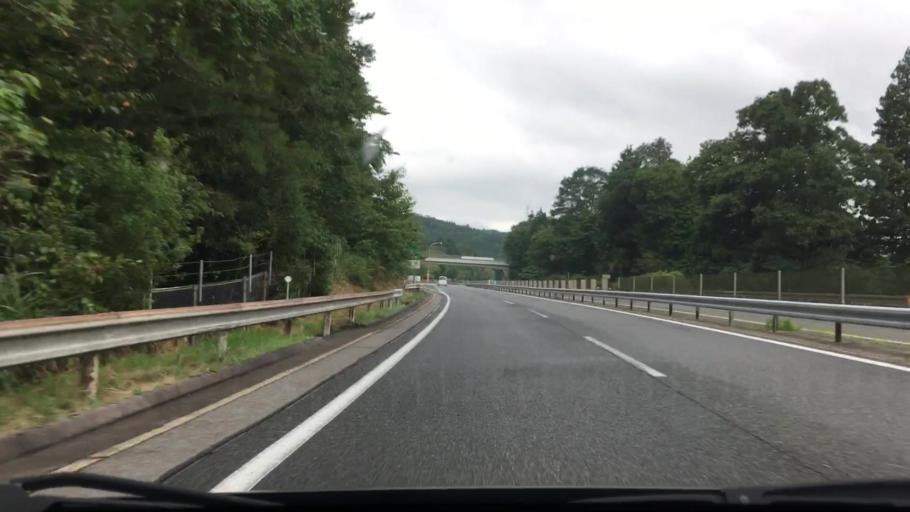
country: JP
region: Hiroshima
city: Miyoshi
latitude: 34.6983
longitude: 132.6034
